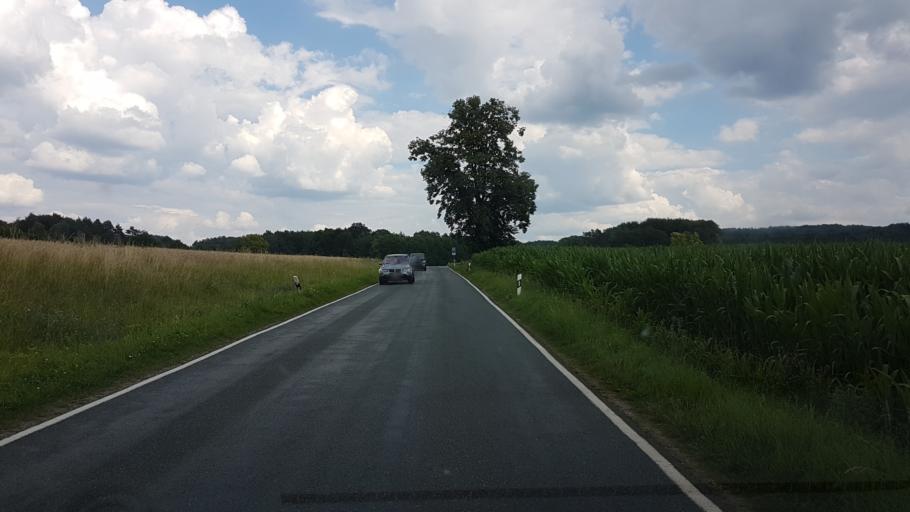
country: DE
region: Bavaria
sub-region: Upper Franconia
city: Gossweinstein
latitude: 49.7648
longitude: 11.3076
